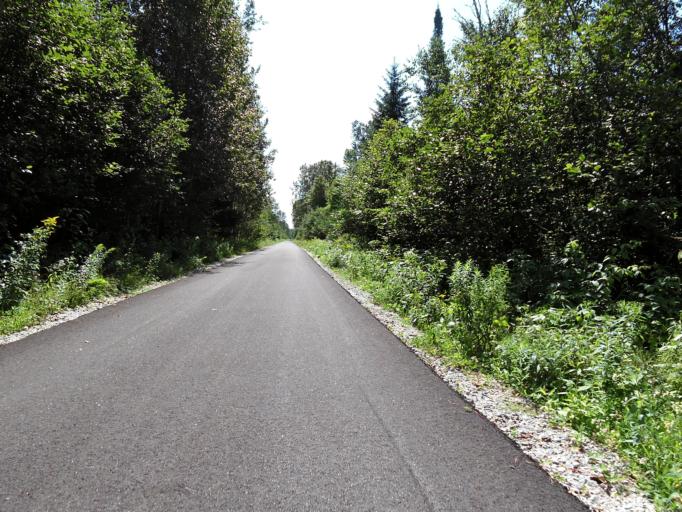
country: CA
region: Quebec
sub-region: Outaouais
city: Maniwaki
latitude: 46.1813
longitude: -76.0430
